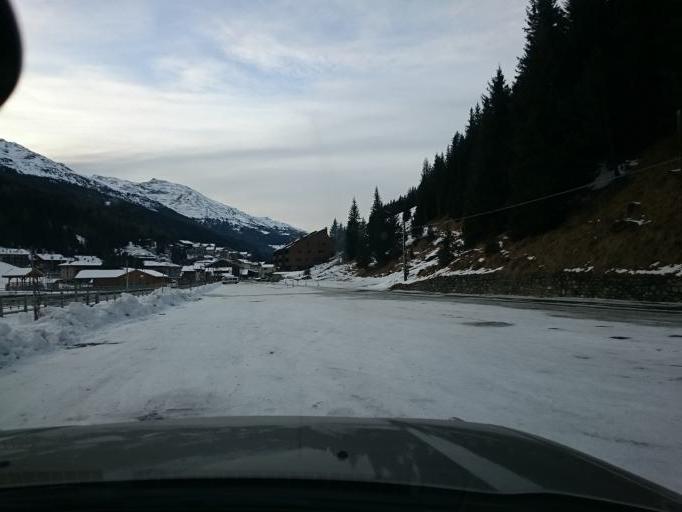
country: IT
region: Lombardy
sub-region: Provincia di Sondrio
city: Sant'Antonio
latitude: 46.4111
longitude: 10.5006
